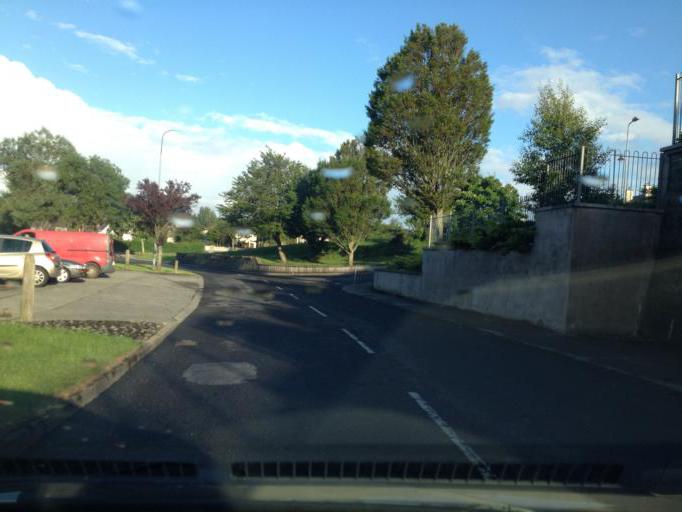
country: IE
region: Connaught
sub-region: Sligo
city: Sligo
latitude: 54.2704
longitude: -8.4602
